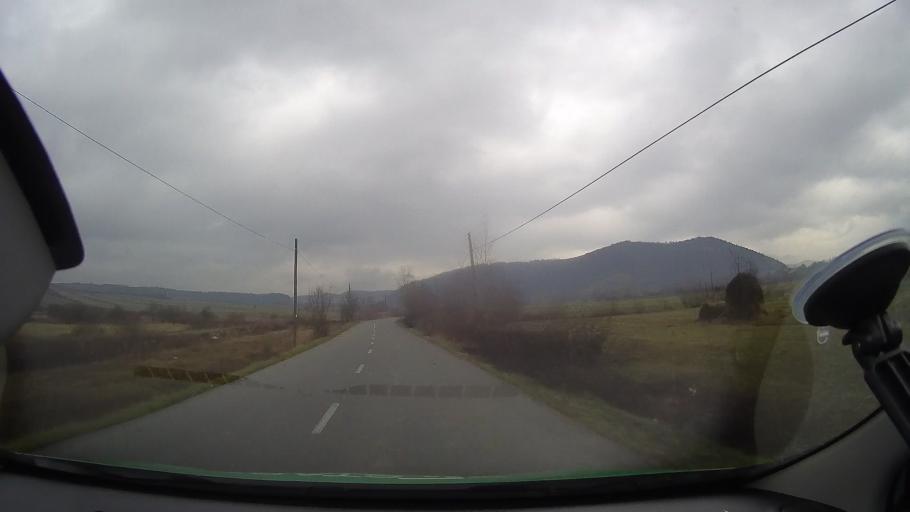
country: RO
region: Hunedoara
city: Vata de Jos
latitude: 46.1905
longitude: 22.6255
